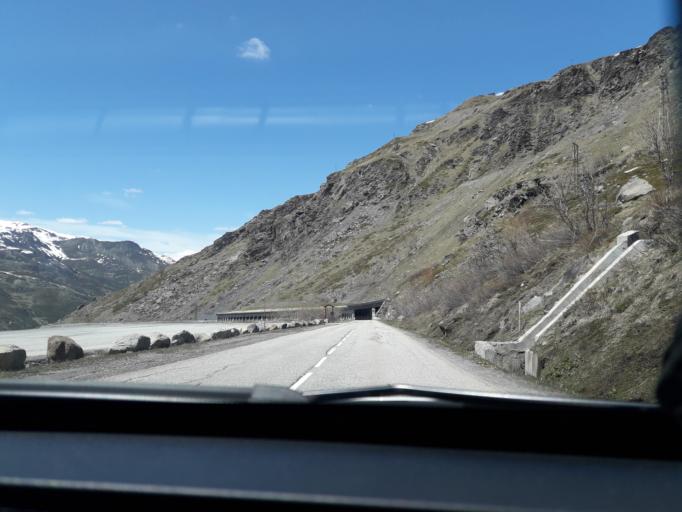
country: FR
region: Rhone-Alpes
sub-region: Departement de la Savoie
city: Val Thorens
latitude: 45.2988
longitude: 6.5645
